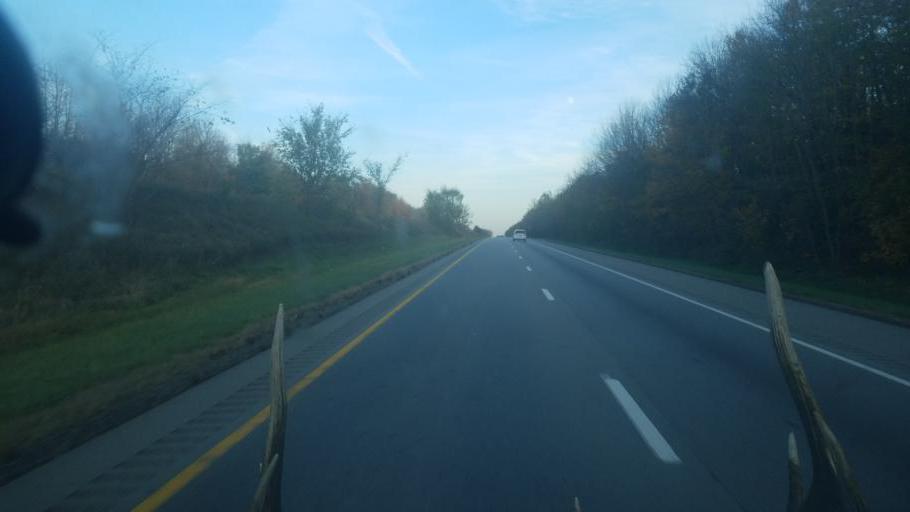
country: US
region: Ohio
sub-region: Muskingum County
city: Zanesville
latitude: 39.9516
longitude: -82.1792
